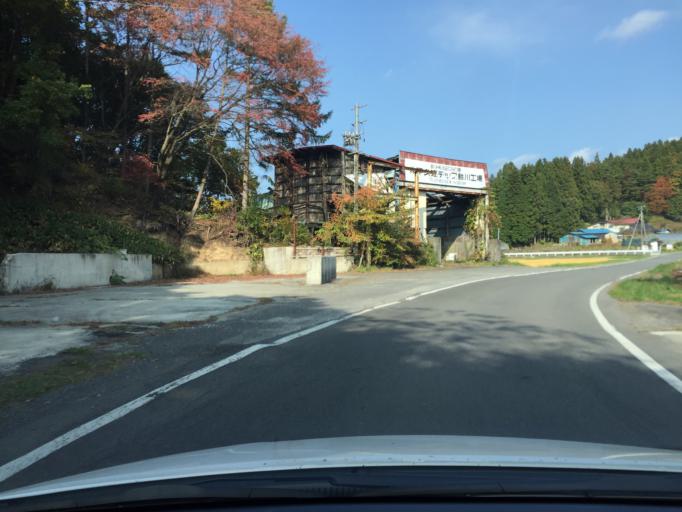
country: JP
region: Fukushima
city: Ishikawa
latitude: 36.9574
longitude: 140.5657
